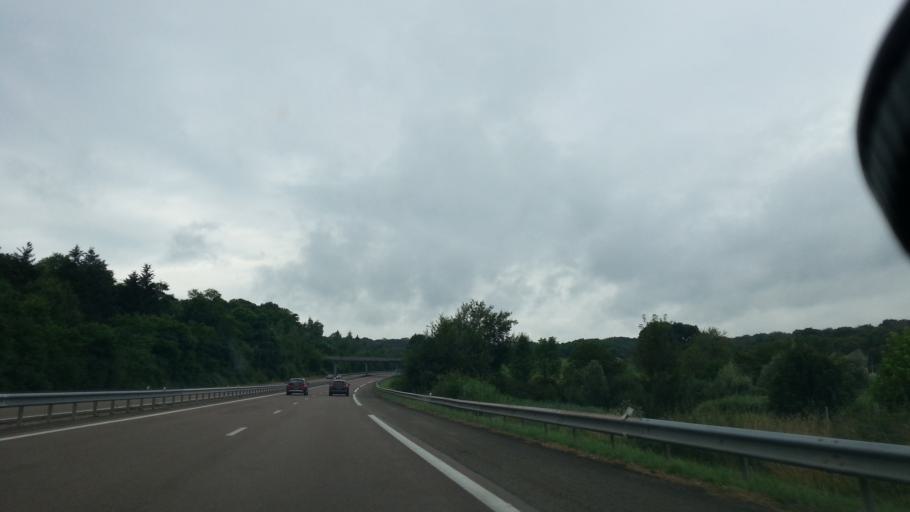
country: FR
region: Franche-Comte
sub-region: Departement du Jura
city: Orchamps
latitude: 47.1547
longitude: 5.6060
